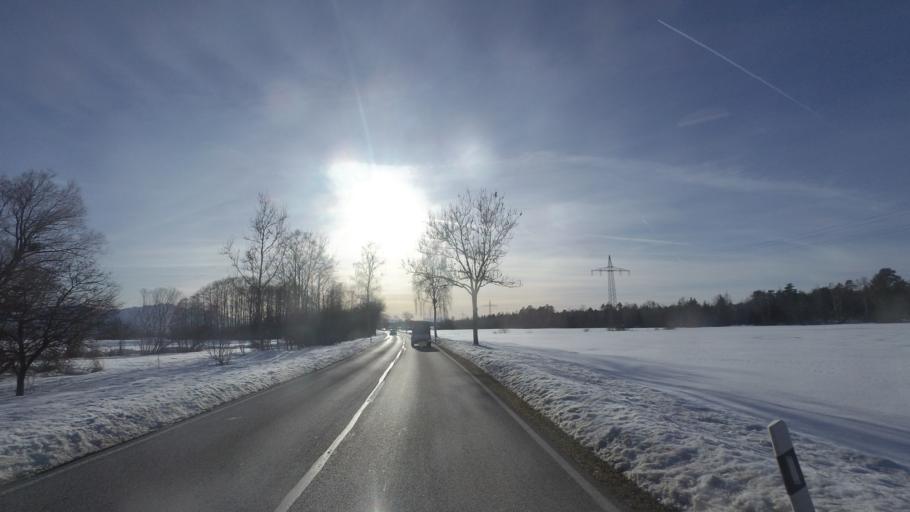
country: DE
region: Bavaria
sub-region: Upper Bavaria
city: Seeon-Seebruck
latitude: 47.9338
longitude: 12.4572
